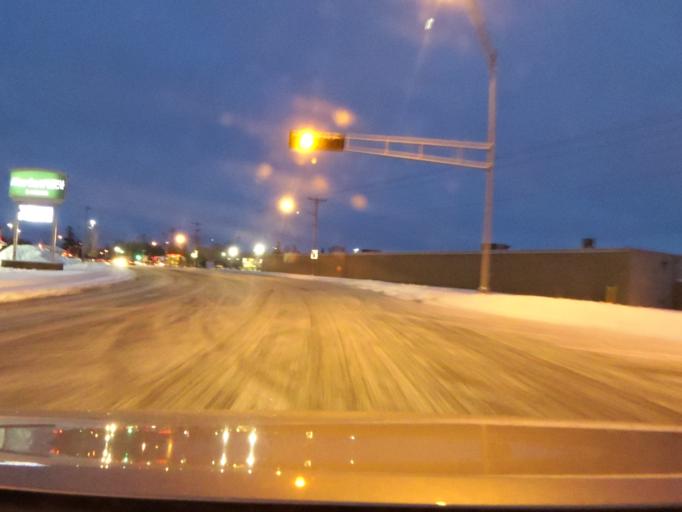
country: US
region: Wisconsin
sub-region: Dunn County
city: Menomonie
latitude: 44.9012
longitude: -91.9350
